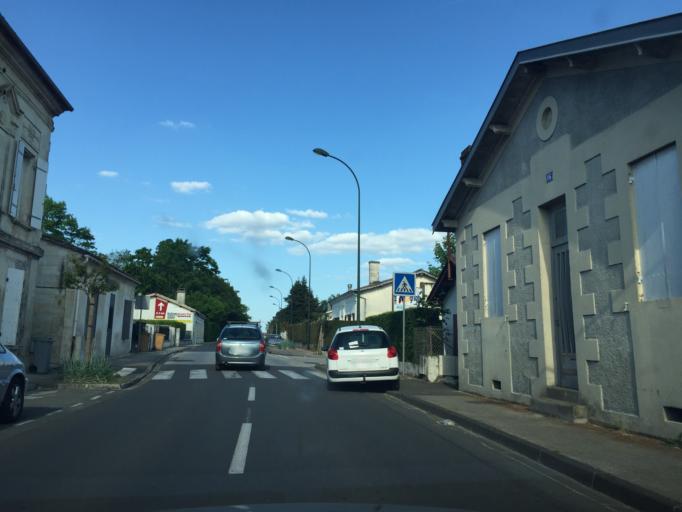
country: FR
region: Aquitaine
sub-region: Departement de la Gironde
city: Coutras
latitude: 45.0365
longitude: -0.1427
